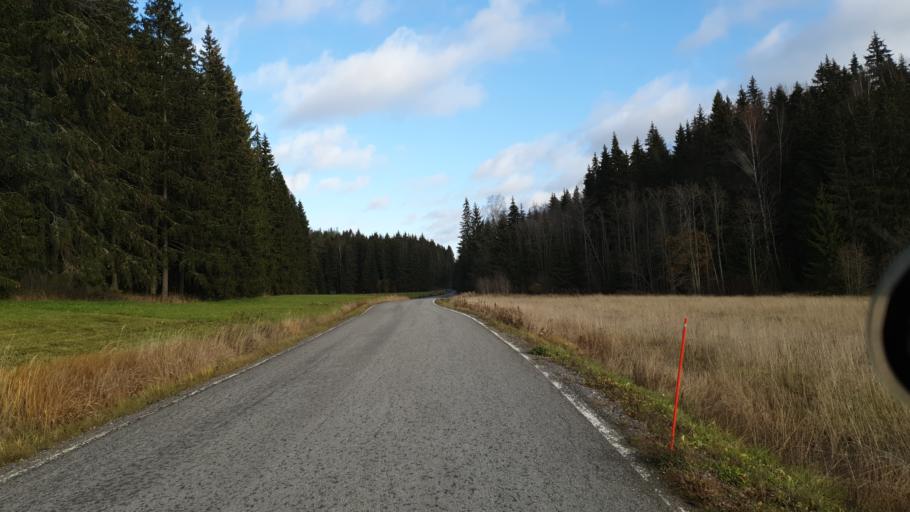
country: FI
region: Uusimaa
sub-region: Helsinki
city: Siuntio
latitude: 60.2608
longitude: 24.3011
